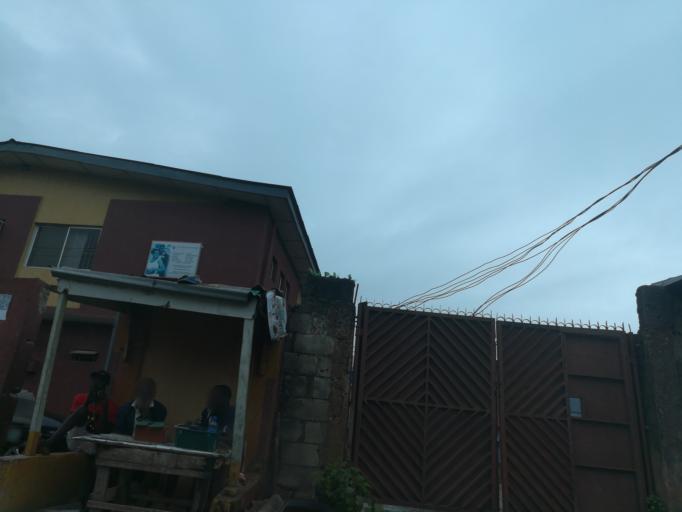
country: NG
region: Lagos
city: Oshodi
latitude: 6.5686
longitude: 3.3392
